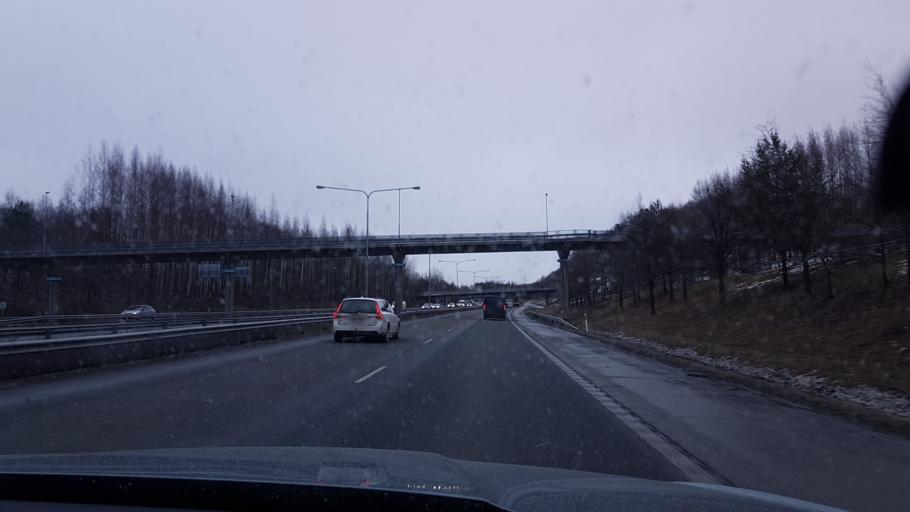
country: FI
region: Pirkanmaa
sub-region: Tampere
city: Tampere
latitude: 61.4703
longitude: 23.8437
